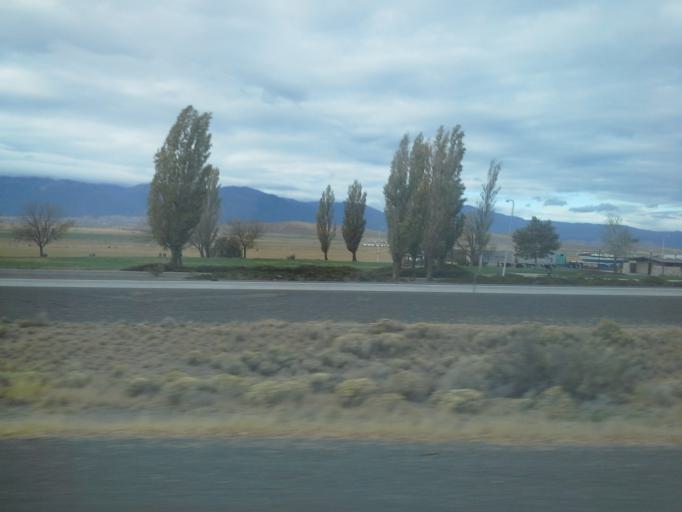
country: US
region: Oregon
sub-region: Baker County
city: Baker City
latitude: 44.9136
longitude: -117.8197
